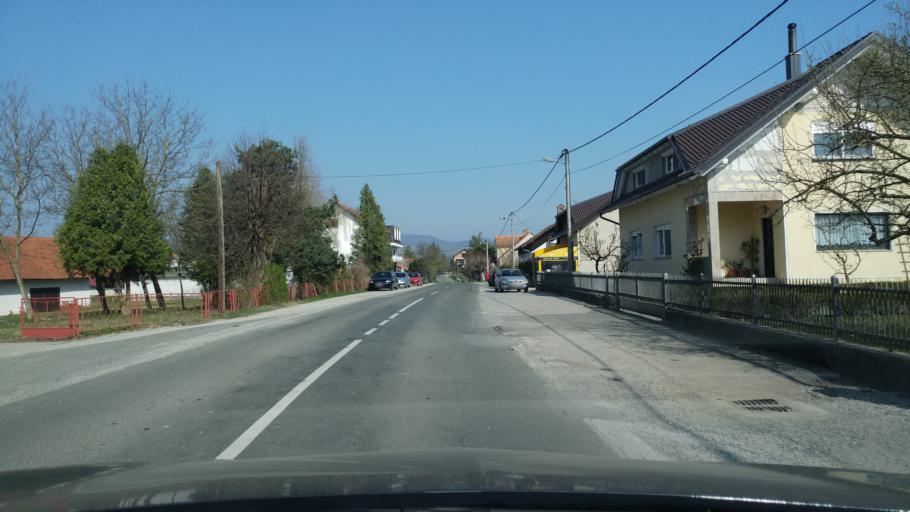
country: SI
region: Bistrica ob Sotli
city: Bistrica ob Sotli
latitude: 45.9882
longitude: 15.7252
